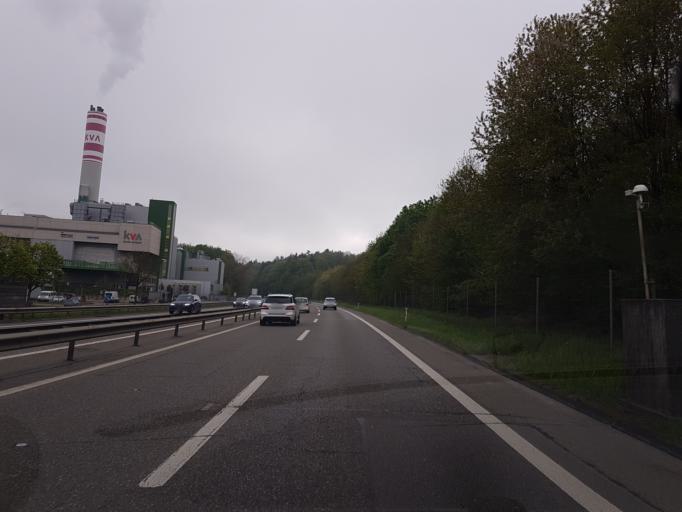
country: CH
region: Aargau
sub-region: Bezirk Aarau
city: Buchs
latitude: 47.3877
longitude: 8.1009
